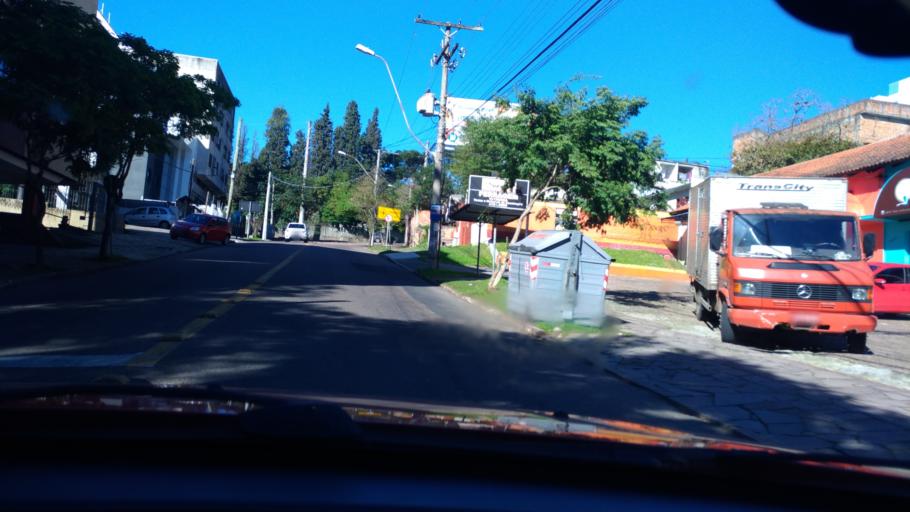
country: BR
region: Rio Grande do Sul
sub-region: Porto Alegre
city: Porto Alegre
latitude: -30.0170
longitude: -51.1816
